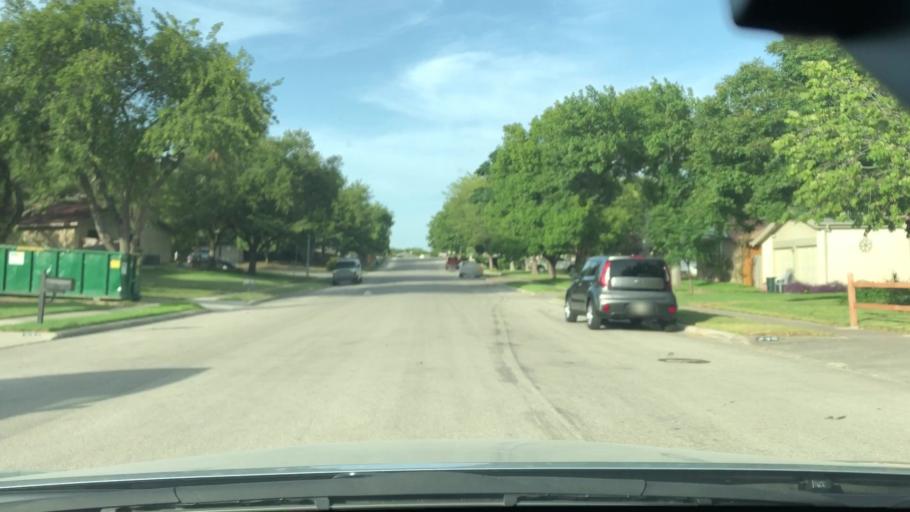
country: US
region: Texas
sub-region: Bexar County
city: Converse
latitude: 29.5344
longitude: -98.3209
